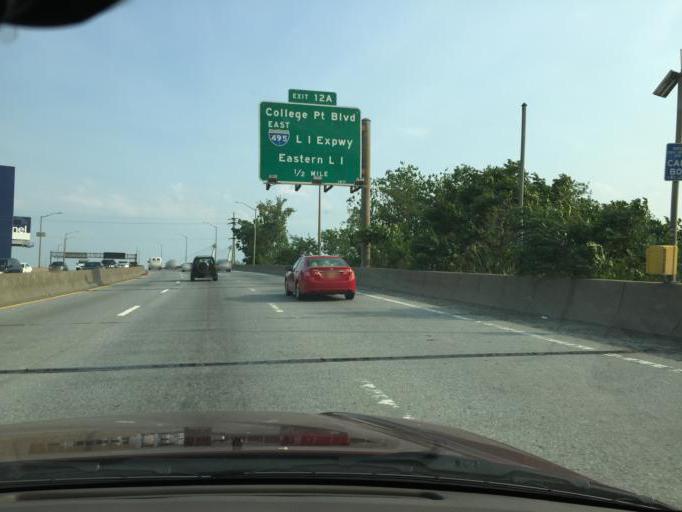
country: US
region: New York
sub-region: Queens County
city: Jamaica
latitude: 40.7556
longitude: -73.8385
